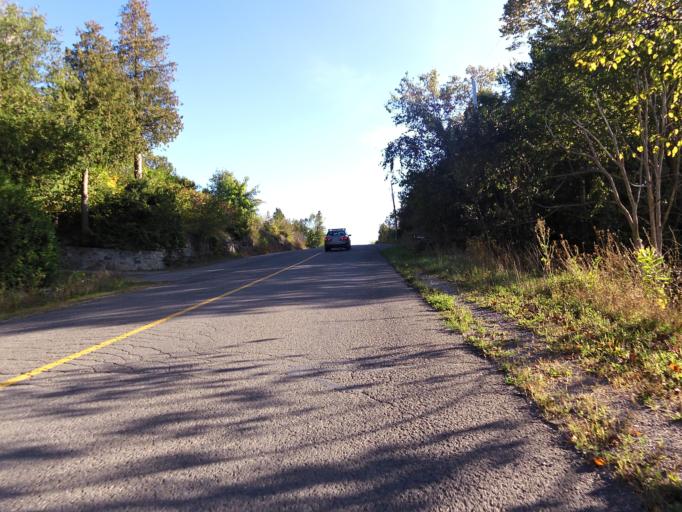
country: CA
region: Ontario
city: Bells Corners
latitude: 45.4493
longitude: -75.8826
